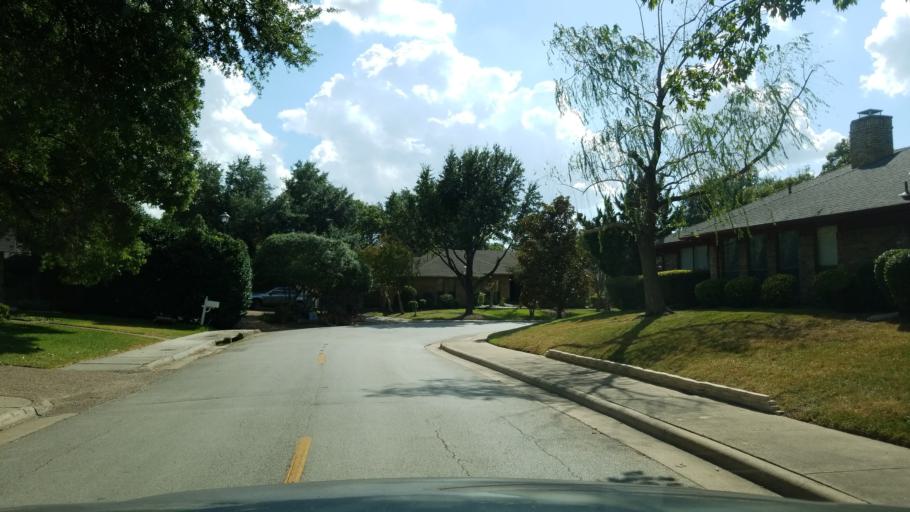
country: US
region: Texas
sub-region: Dallas County
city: Addison
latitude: 32.9701
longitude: -96.7936
